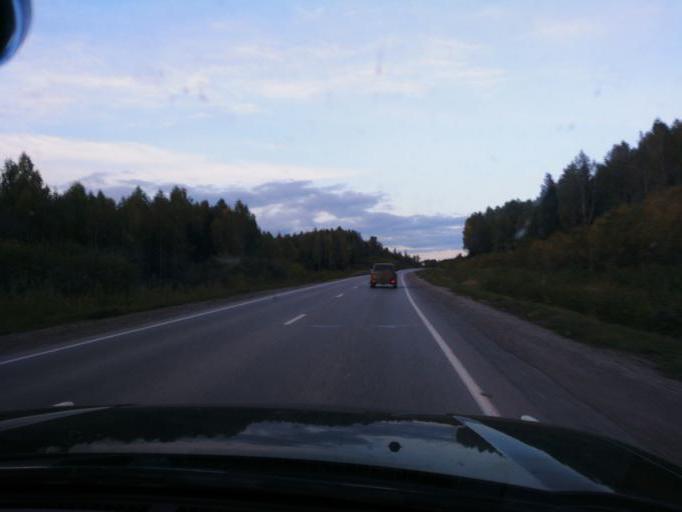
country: RU
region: Perm
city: Polazna
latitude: 58.3001
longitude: 56.5350
